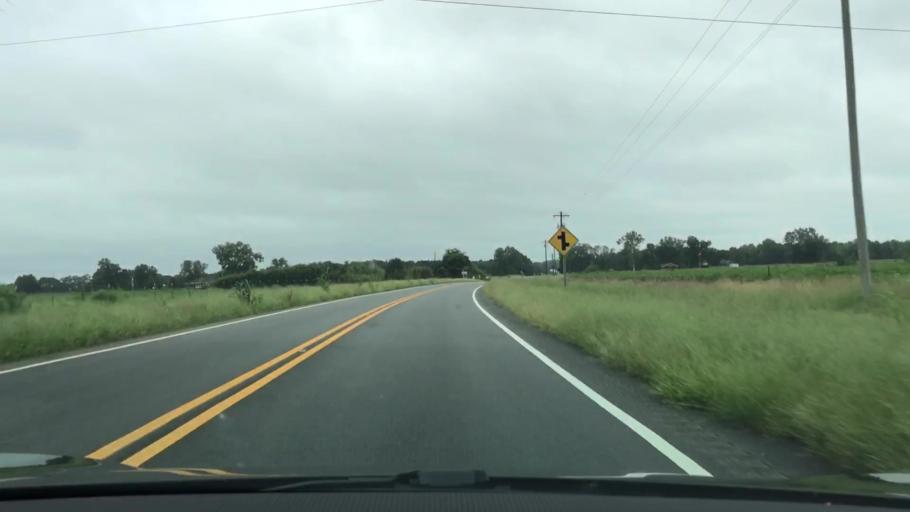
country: US
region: Alabama
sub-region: Covington County
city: Opp
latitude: 31.2371
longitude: -86.1620
